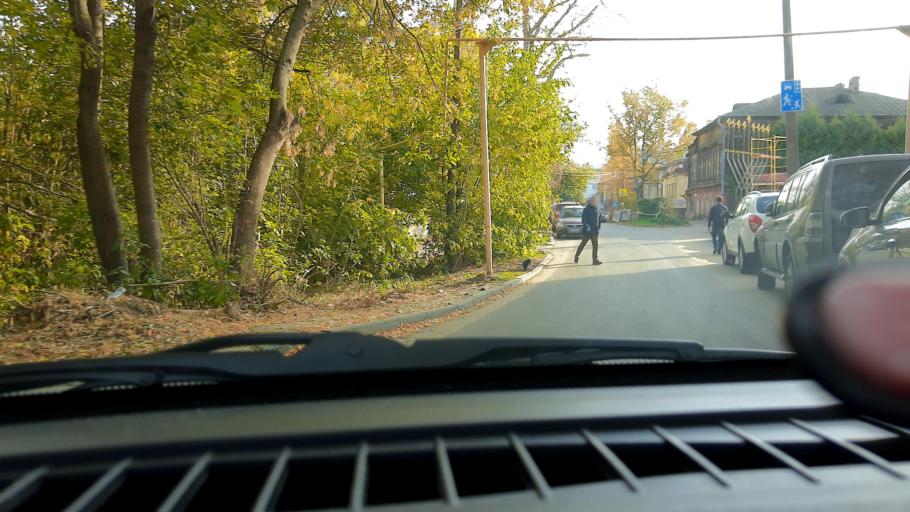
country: RU
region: Nizjnij Novgorod
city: Nizhniy Novgorod
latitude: 56.3206
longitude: 43.9940
